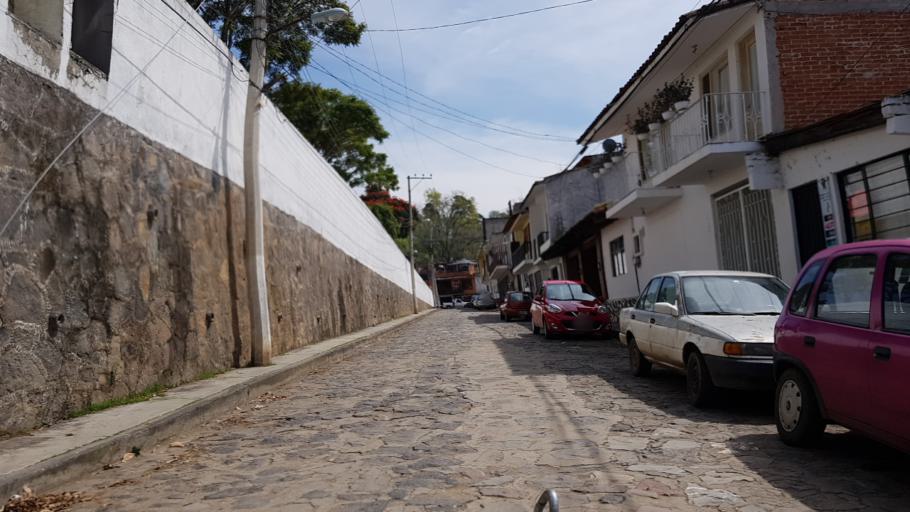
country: MX
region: Mexico
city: Valle de Bravo
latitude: 19.2027
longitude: -100.1368
